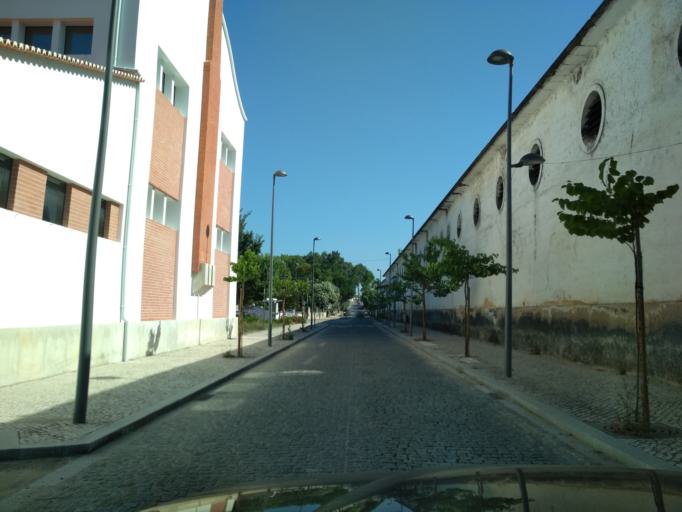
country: PT
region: Aveiro
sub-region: Mealhada
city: Mealhada
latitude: 40.3732
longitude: -8.4534
